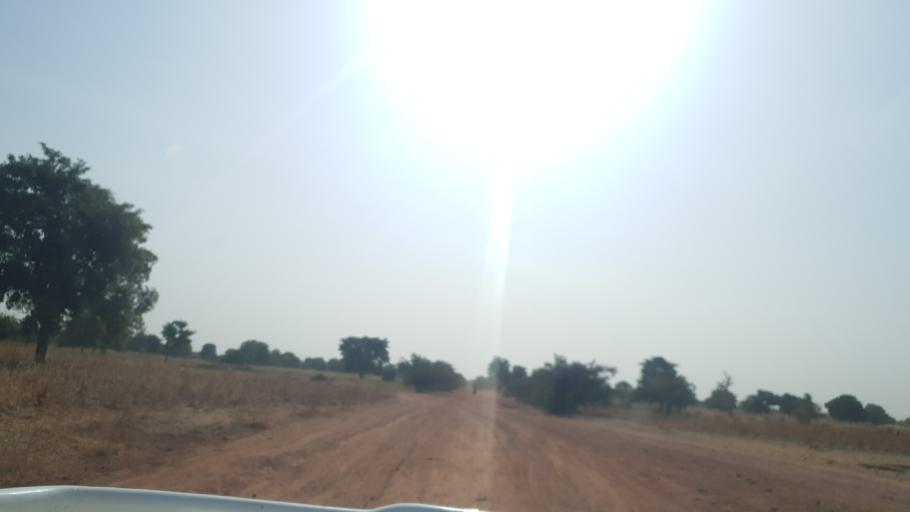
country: ML
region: Koulikoro
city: Dioila
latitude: 12.6989
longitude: -6.7602
